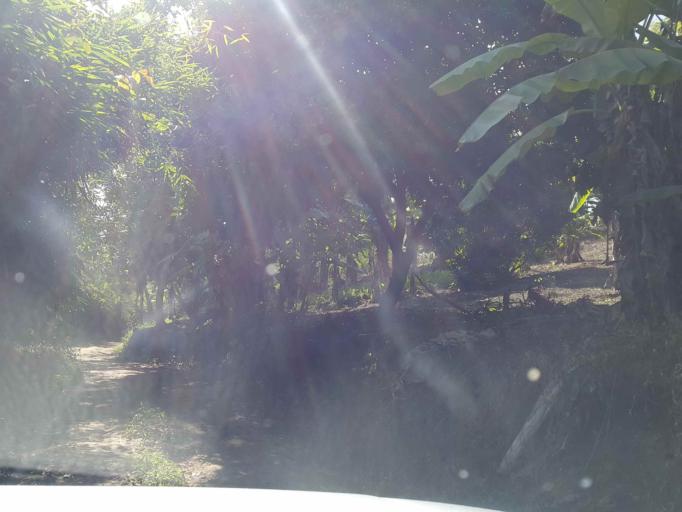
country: TH
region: Chiang Mai
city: Mae Taeng
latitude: 18.9760
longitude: 98.8821
